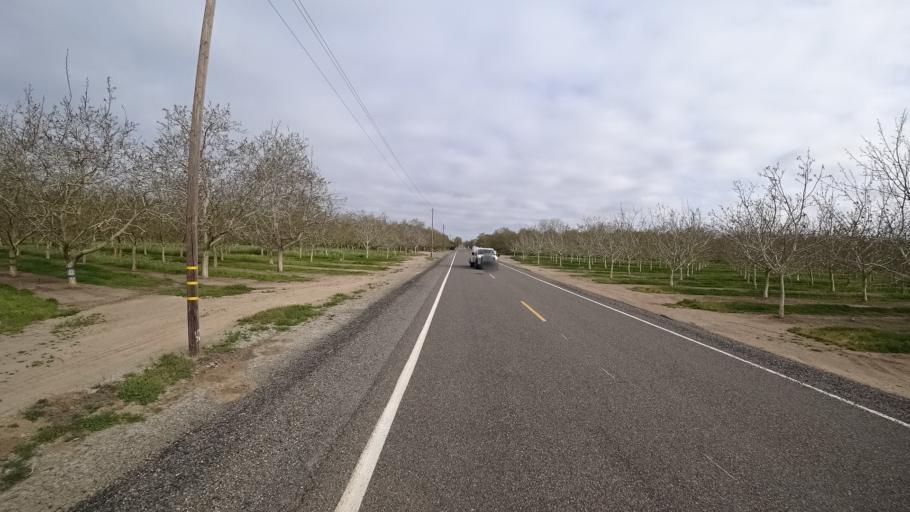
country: US
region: California
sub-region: Colusa County
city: Colusa
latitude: 39.3974
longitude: -121.9969
